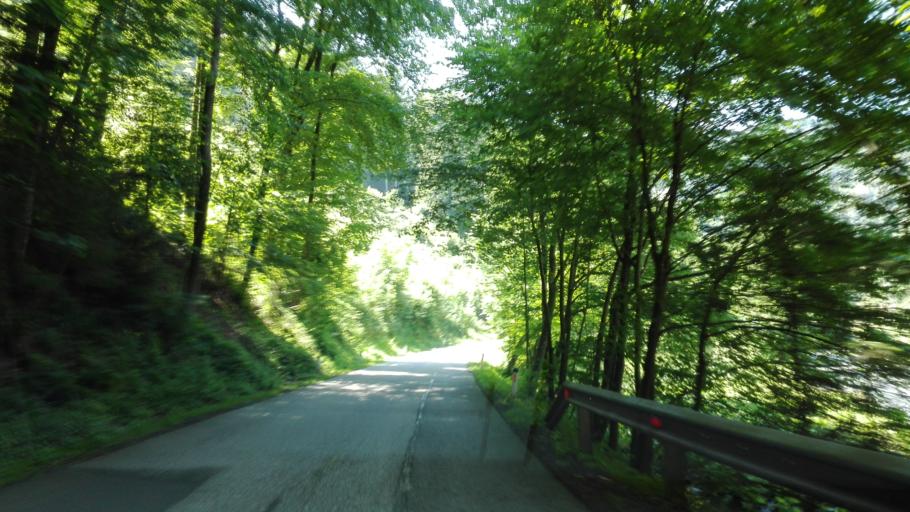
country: AT
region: Upper Austria
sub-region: Politischer Bezirk Rohrbach
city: Kleinzell im Muehlkreis
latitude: 48.3866
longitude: 13.9231
